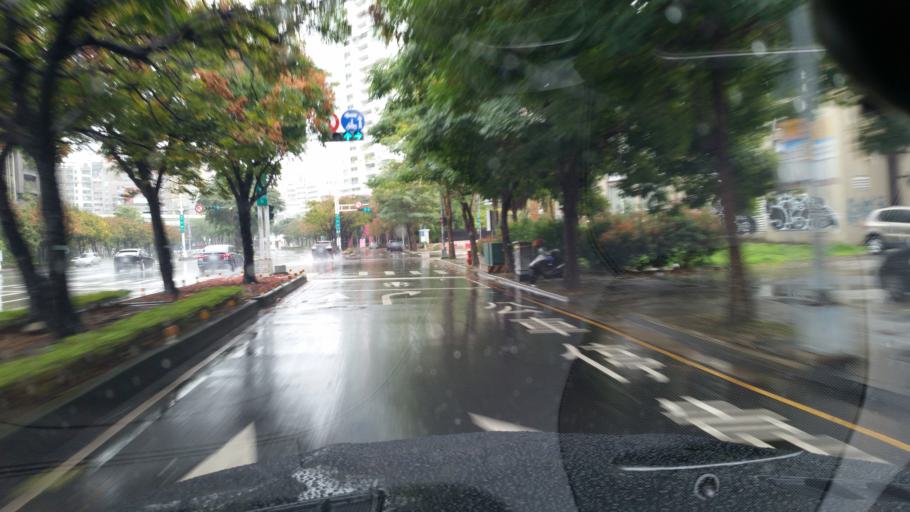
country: TW
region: Taiwan
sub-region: Taichung City
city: Taichung
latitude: 24.1564
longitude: 120.6434
